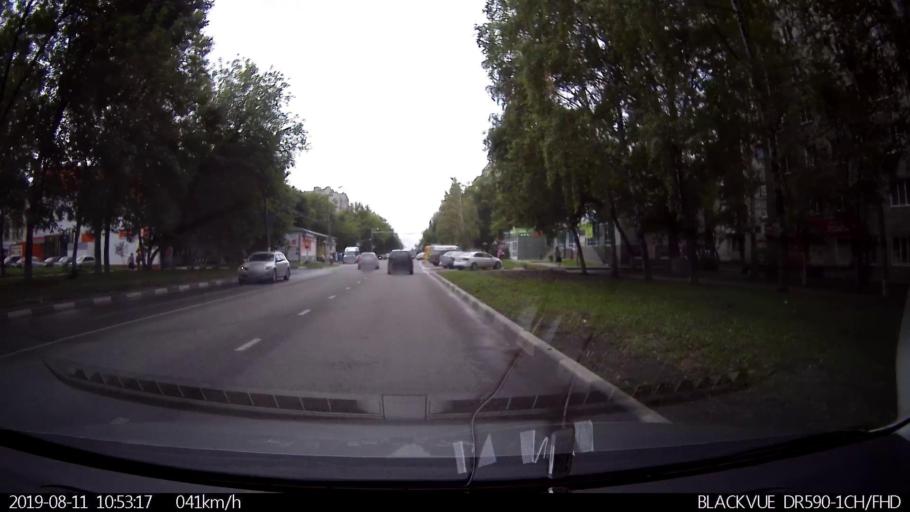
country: RU
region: Ulyanovsk
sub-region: Ulyanovskiy Rayon
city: Ulyanovsk
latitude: 54.2604
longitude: 48.3343
